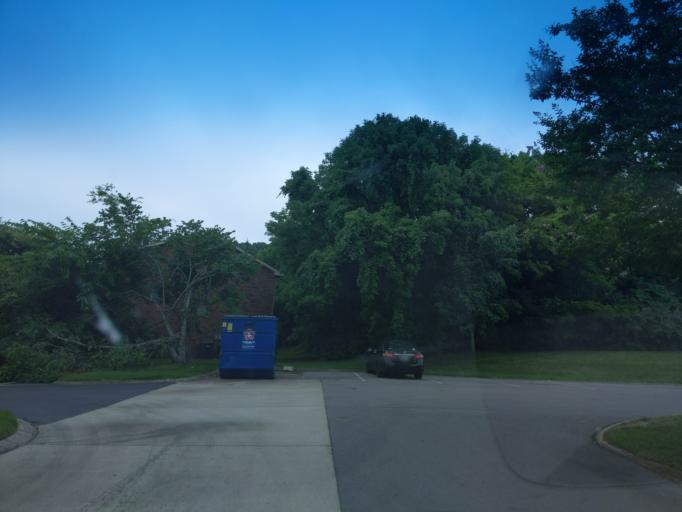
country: US
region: Tennessee
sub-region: Williamson County
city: Brentwood
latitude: 36.0401
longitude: -86.7771
